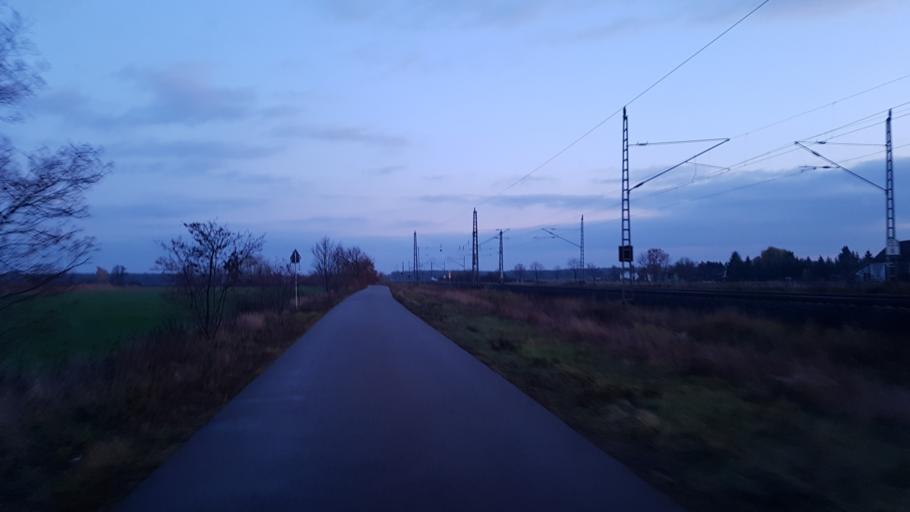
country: DE
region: Brandenburg
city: Falkenberg
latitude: 51.6256
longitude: 13.2030
